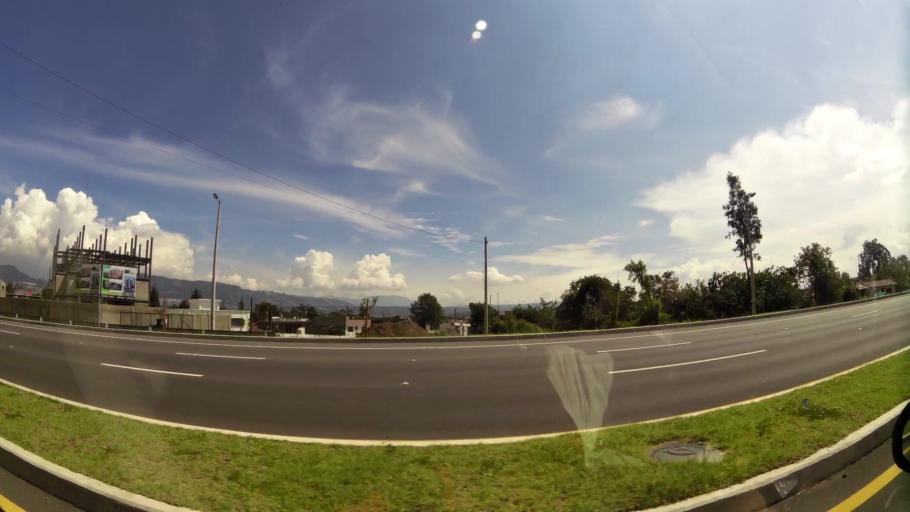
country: EC
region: Pichincha
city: Sangolqui
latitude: -0.2224
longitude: -78.4017
